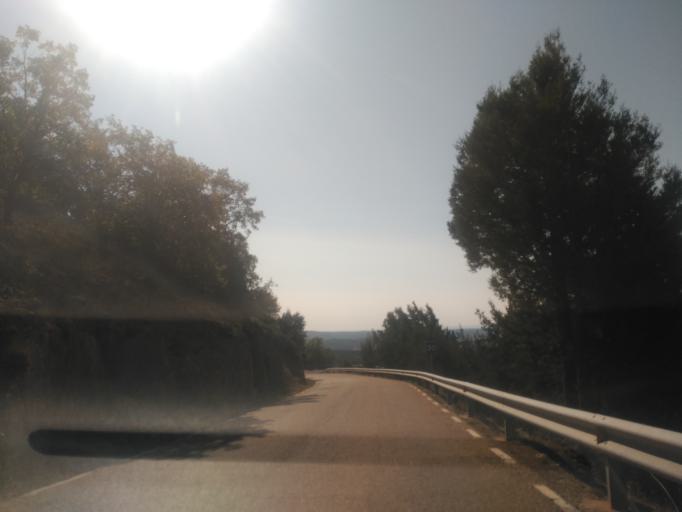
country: ES
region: Castille and Leon
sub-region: Provincia de Soria
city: Ucero
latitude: 41.7295
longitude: -3.0415
